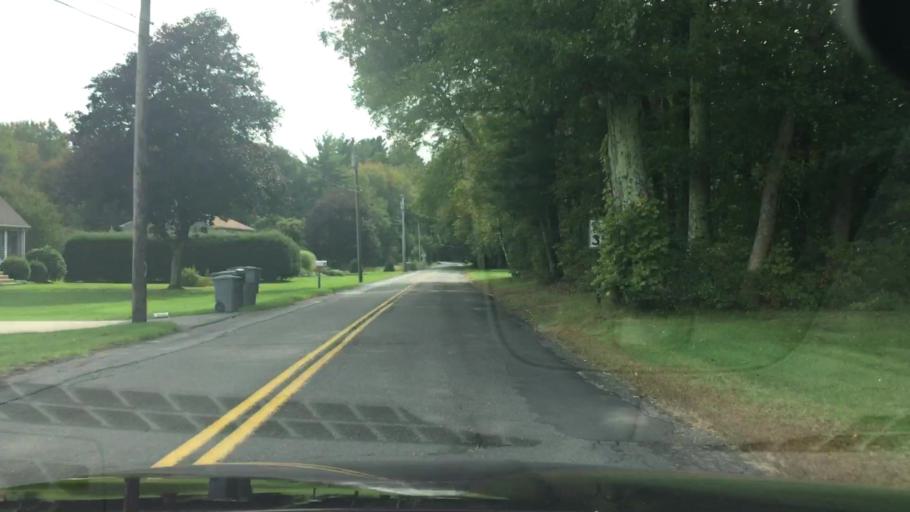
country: US
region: Connecticut
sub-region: Hartford County
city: Hazardville
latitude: 42.0056
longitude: -72.5096
